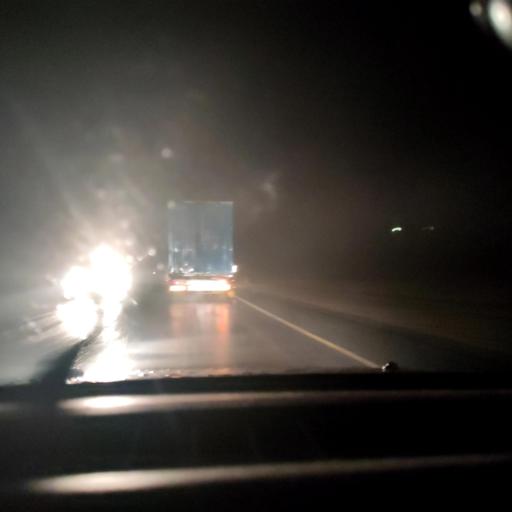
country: RU
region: Voronezj
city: Latnaya
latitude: 51.6444
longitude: 38.8368
